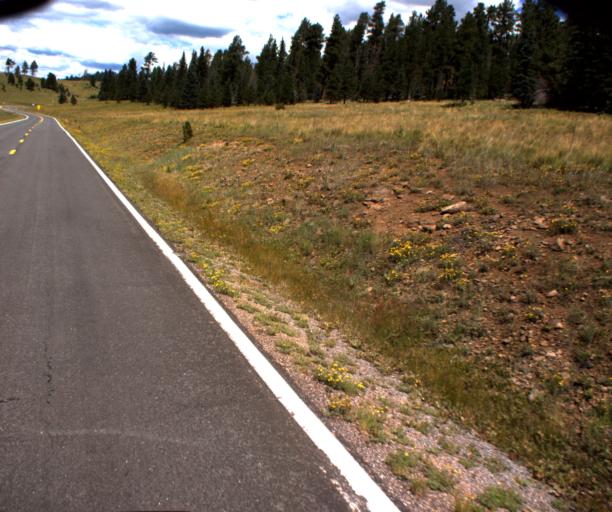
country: US
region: Arizona
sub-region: Apache County
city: Eagar
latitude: 33.8883
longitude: -109.4023
